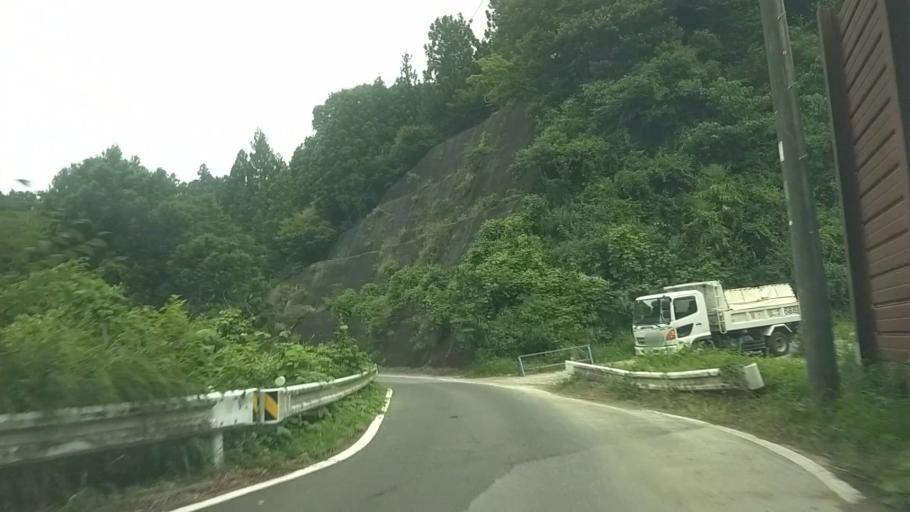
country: JP
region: Chiba
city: Kawaguchi
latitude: 35.2152
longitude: 140.1374
